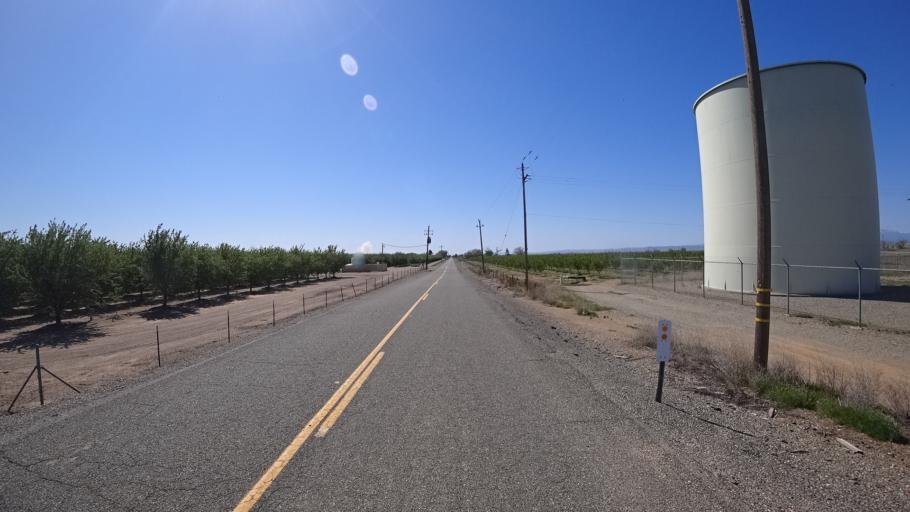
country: US
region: California
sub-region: Glenn County
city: Orland
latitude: 39.6450
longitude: -122.2533
